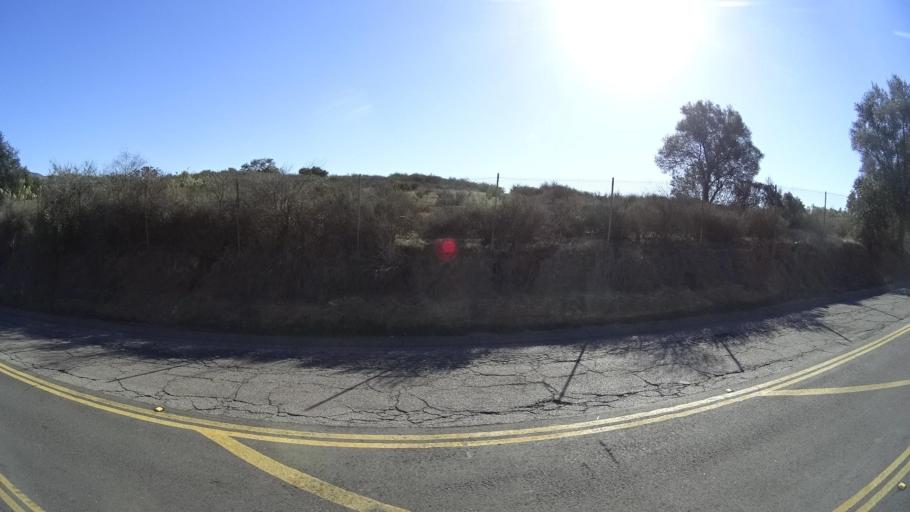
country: US
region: California
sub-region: San Diego County
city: Jamul
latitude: 32.7200
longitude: -116.8755
